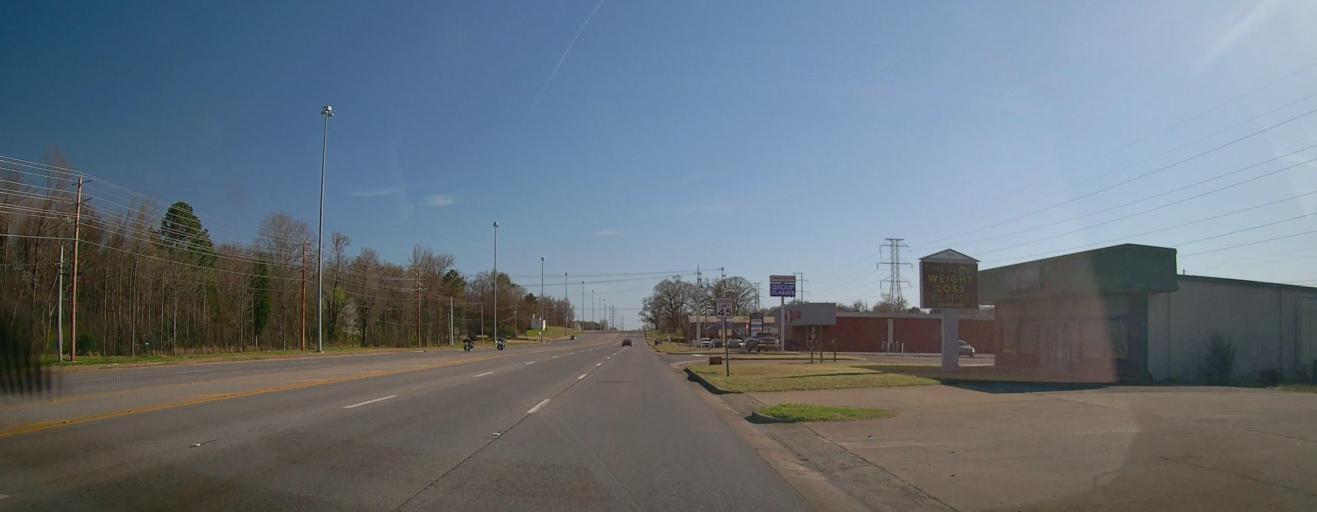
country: US
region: Alabama
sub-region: Colbert County
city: Muscle Shoals
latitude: 34.7580
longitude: -87.6350
